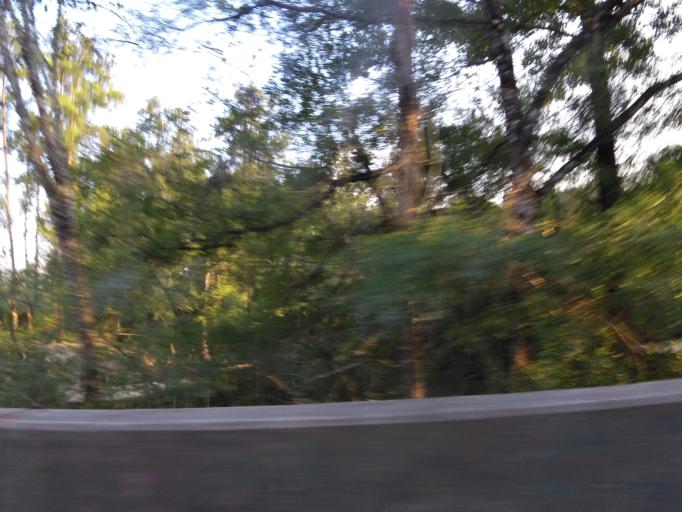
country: US
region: Florida
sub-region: Duval County
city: Baldwin
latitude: 30.3849
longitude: -82.0361
